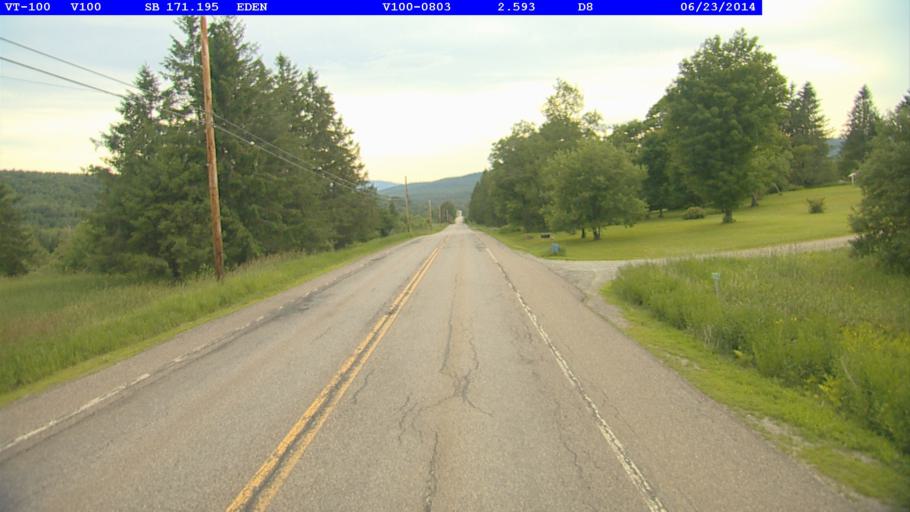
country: US
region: Vermont
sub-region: Lamoille County
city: Hyde Park
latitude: 44.7057
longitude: -72.5512
